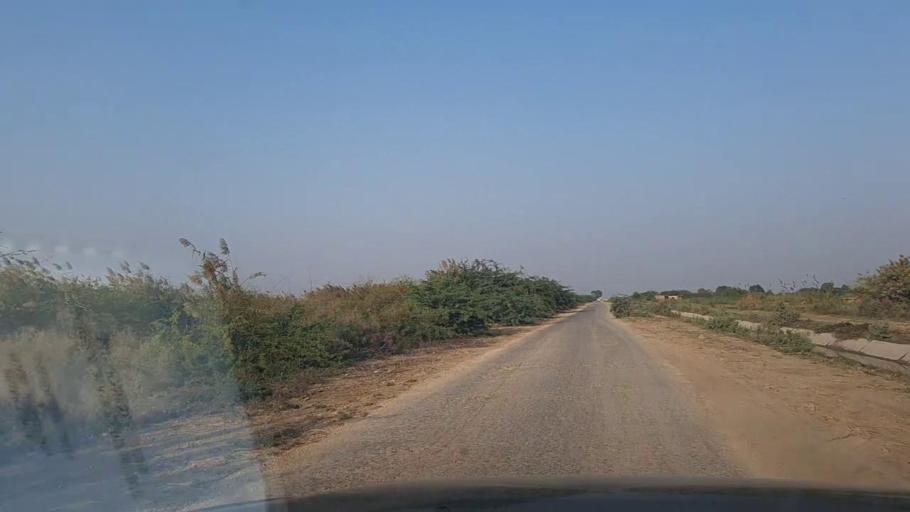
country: PK
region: Sindh
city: Keti Bandar
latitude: 24.2573
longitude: 67.5397
